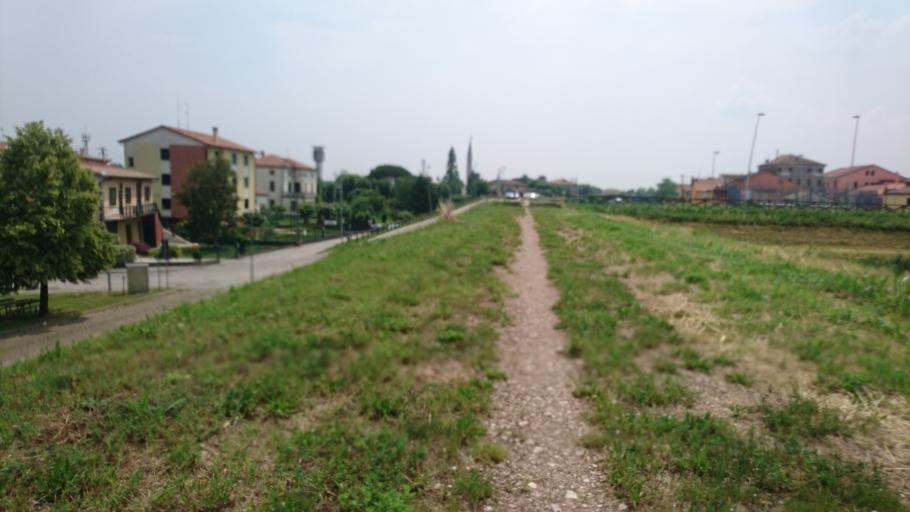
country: IT
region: Veneto
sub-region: Provincia di Padova
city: Bovolenta
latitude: 45.2718
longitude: 11.9351
